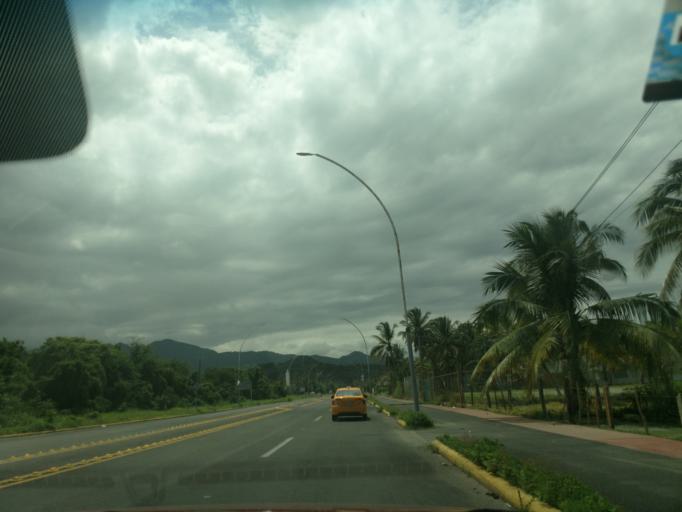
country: MX
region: Nayarit
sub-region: San Blas
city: Aticama
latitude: 21.5028
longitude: -105.2050
